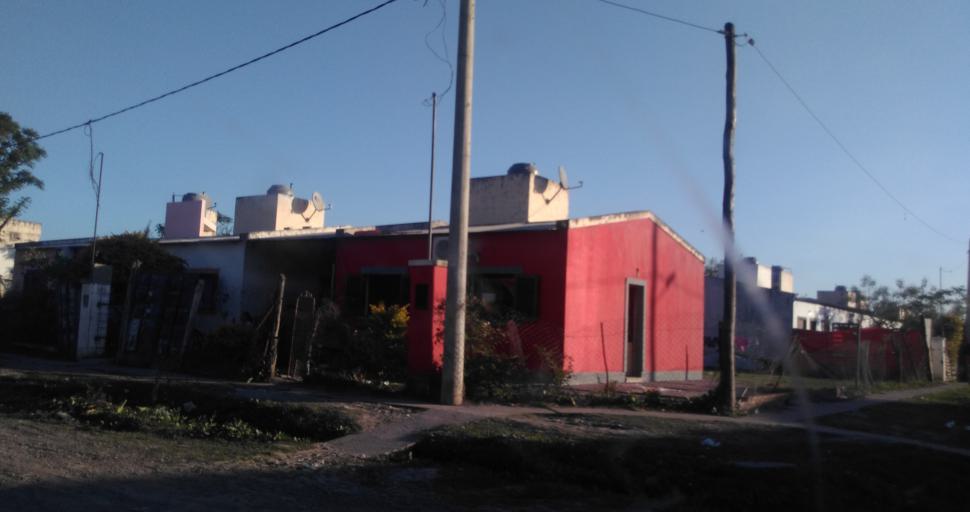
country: AR
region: Chaco
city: Fontana
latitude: -27.4662
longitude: -59.0359
